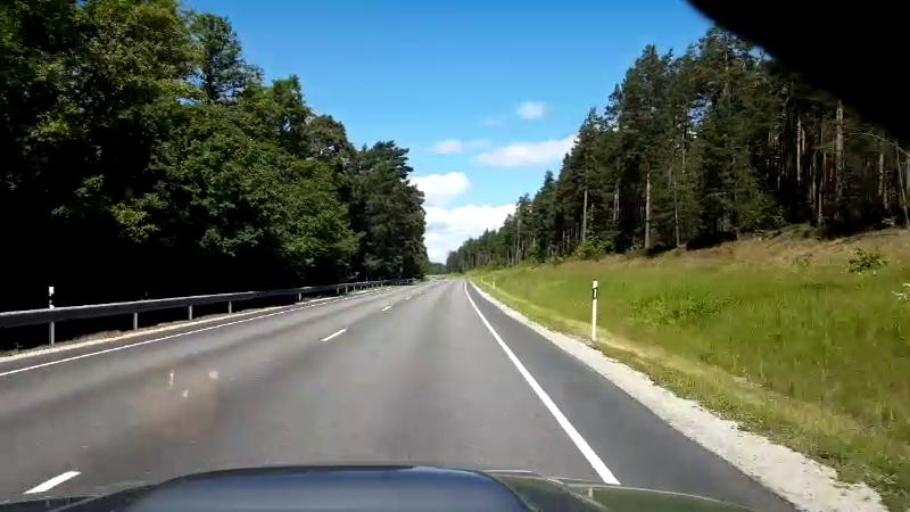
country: EE
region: Paernumaa
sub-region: Paernu linn
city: Parnu
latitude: 58.1710
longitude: 24.4952
